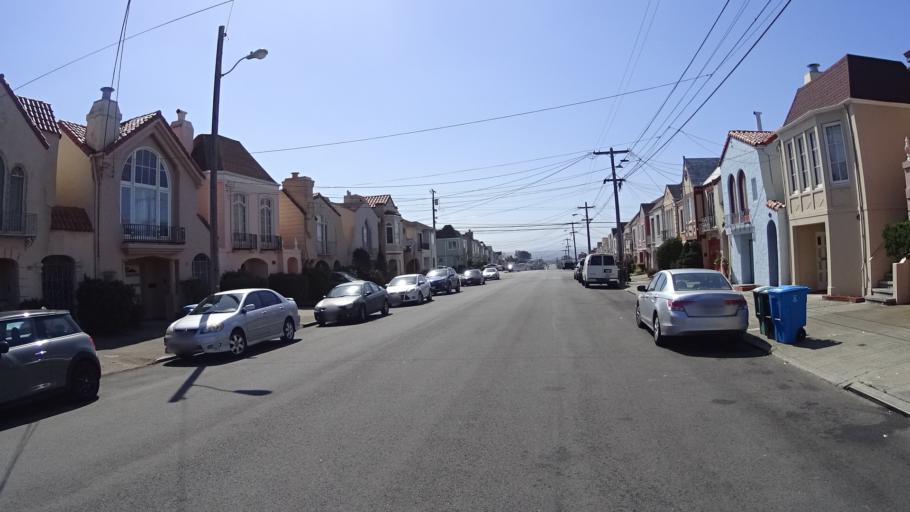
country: US
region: California
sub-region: San Mateo County
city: Daly City
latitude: 37.7562
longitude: -122.4906
